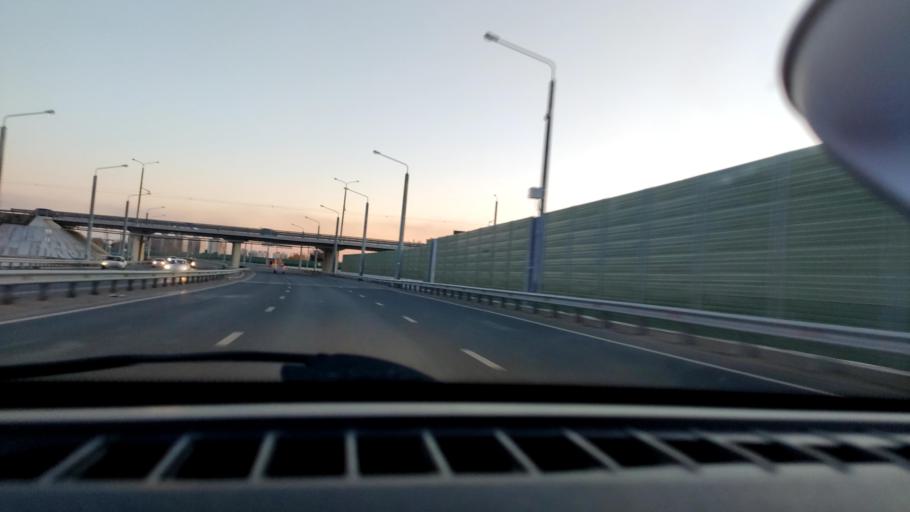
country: RU
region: Samara
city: Samara
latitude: 53.1666
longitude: 50.0852
